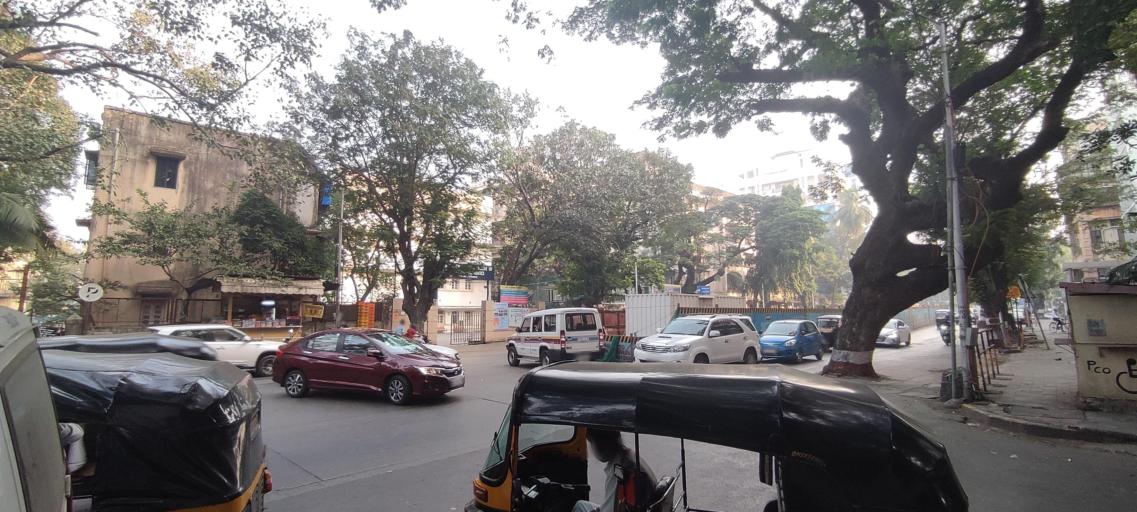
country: IN
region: Maharashtra
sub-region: Mumbai Suburban
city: Mumbai
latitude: 19.0726
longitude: 72.8374
